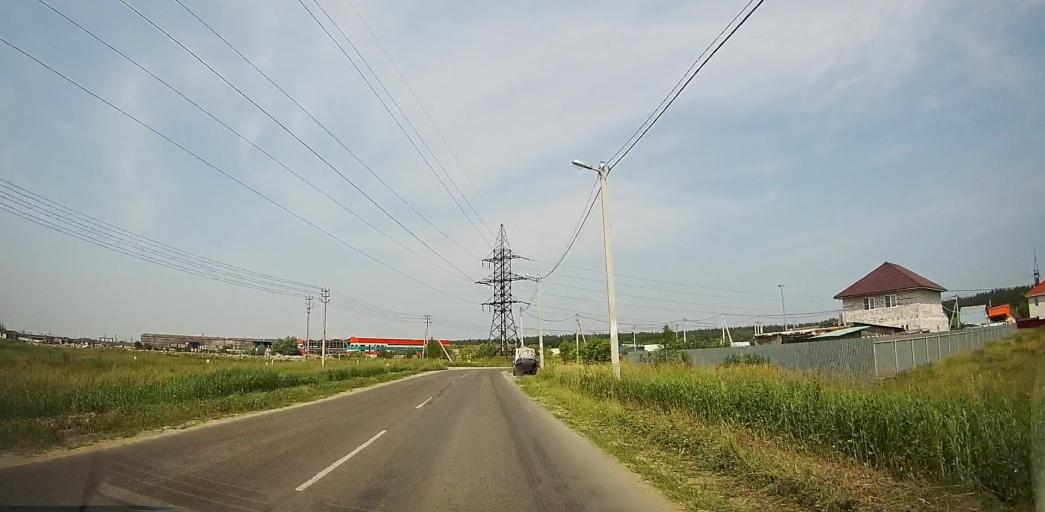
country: RU
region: Moskovskaya
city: Malyshevo
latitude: 55.5030
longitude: 38.3234
